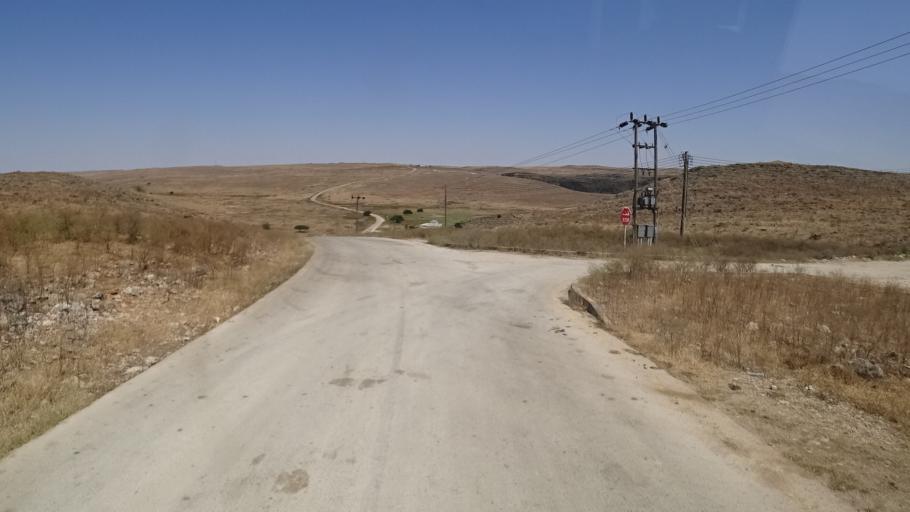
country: OM
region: Zufar
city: Salalah
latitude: 17.1482
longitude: 54.6176
